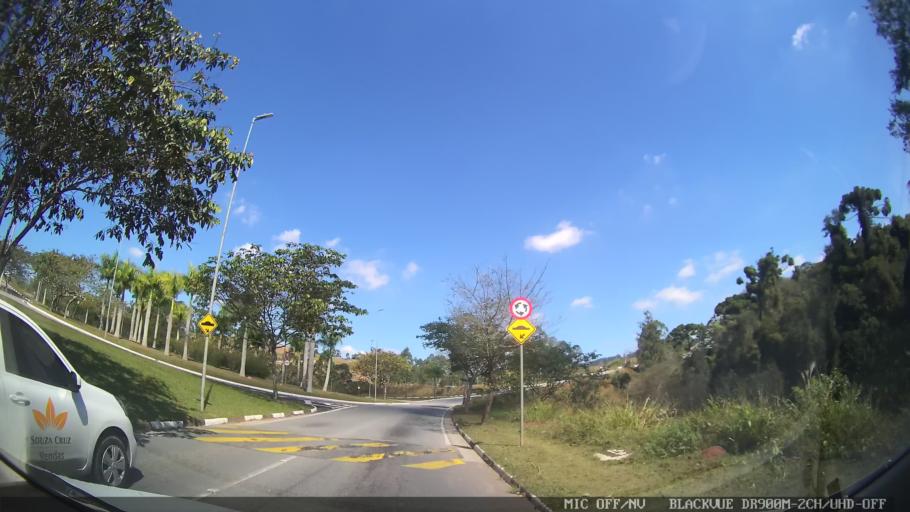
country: BR
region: Sao Paulo
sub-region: Carapicuiba
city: Carapicuiba
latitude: -23.4411
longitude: -46.8328
